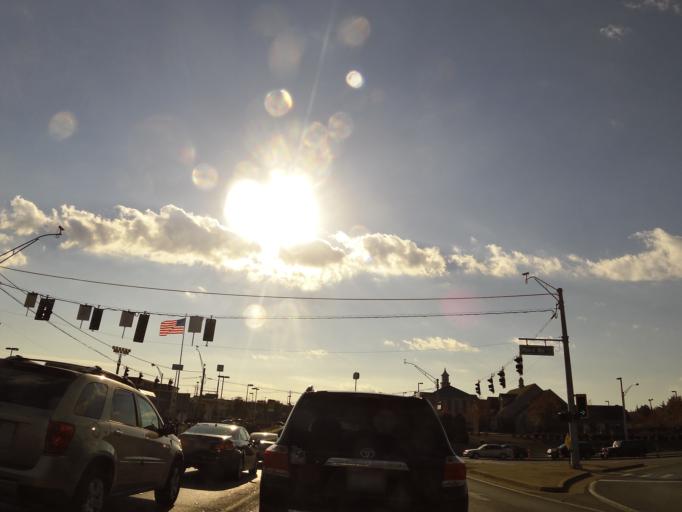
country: US
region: Kentucky
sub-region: Fayette County
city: Lexington-Fayette
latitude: 38.0195
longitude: -84.4173
